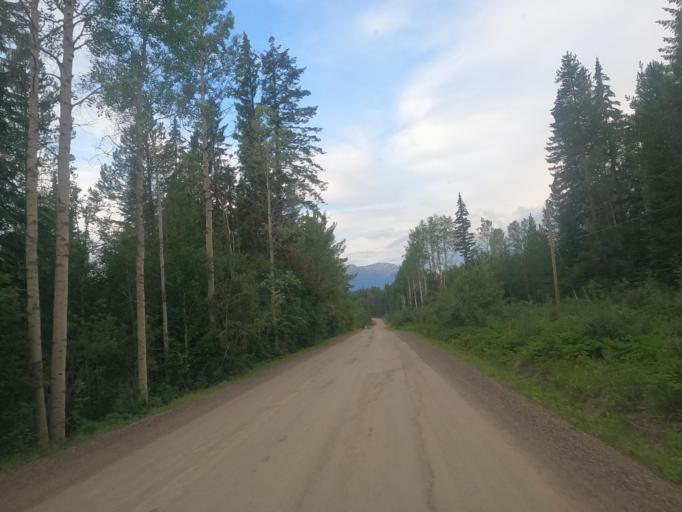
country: CA
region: British Columbia
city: Golden
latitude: 51.4459
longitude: -117.0166
